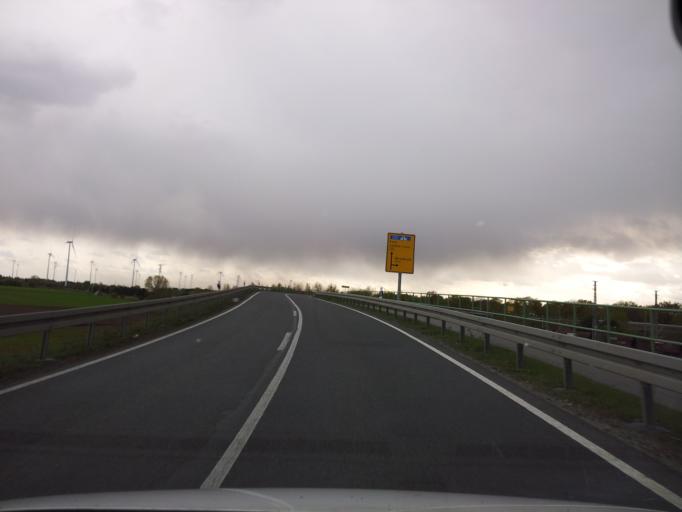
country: DE
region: Brandenburg
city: Heinersbruck
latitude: 51.8055
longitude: 14.4960
